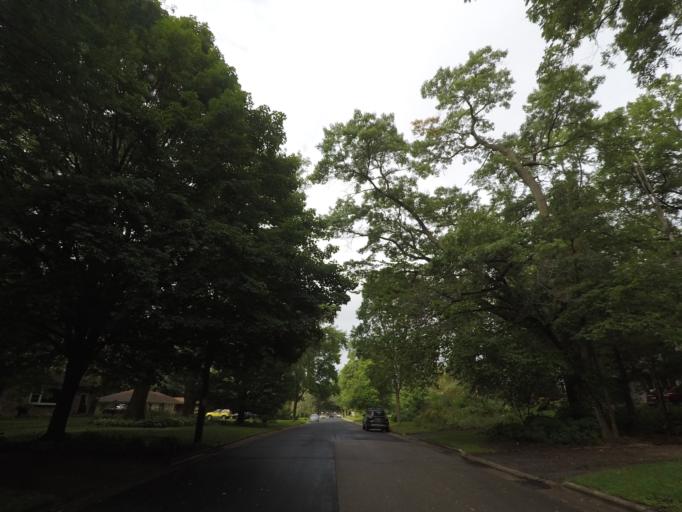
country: US
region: Wisconsin
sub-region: Dane County
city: Shorewood Hills
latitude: 43.0369
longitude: -89.4750
